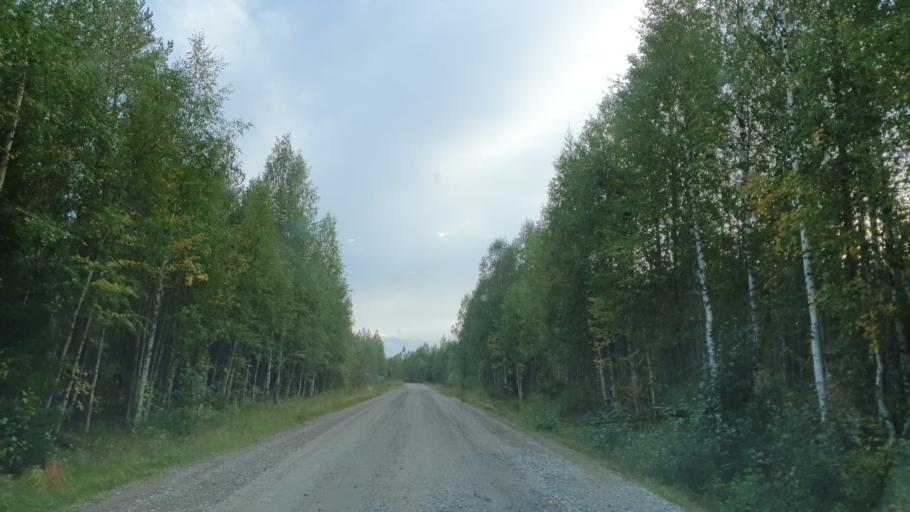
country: FI
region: Kainuu
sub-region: Kehys-Kainuu
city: Kuhmo
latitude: 64.3818
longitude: 29.5539
